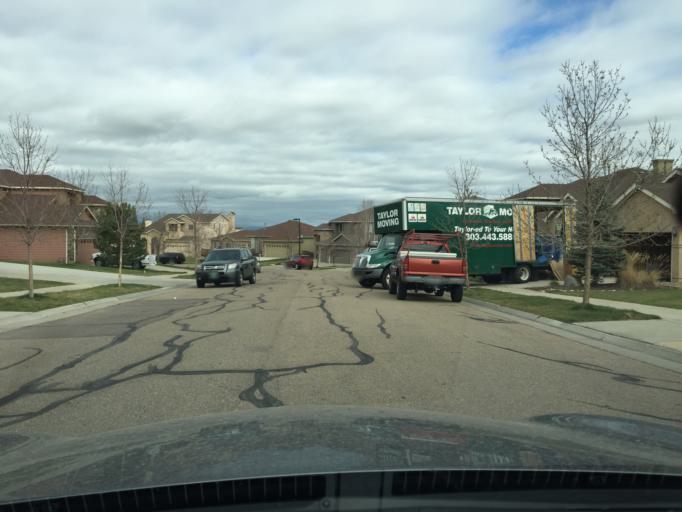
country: US
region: Colorado
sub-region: Boulder County
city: Erie
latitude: 40.0102
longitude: -105.0127
